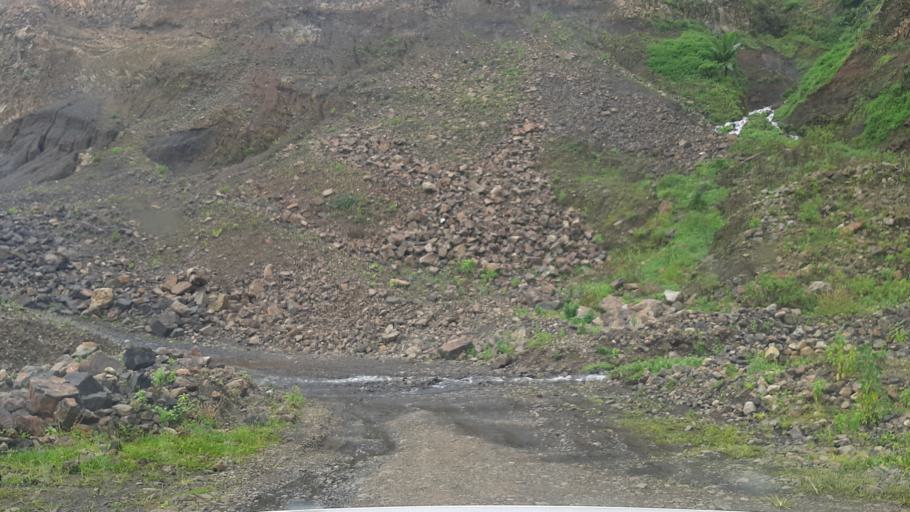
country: ET
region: Southern Nations, Nationalities, and People's Region
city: Bonga
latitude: 7.1414
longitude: 36.5670
